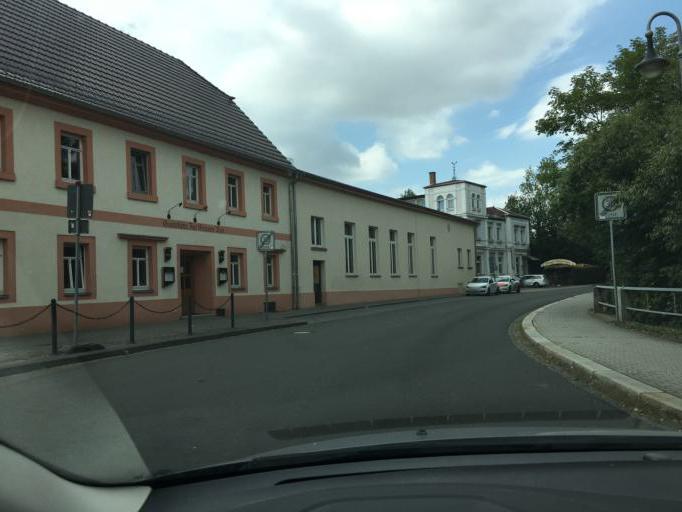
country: DE
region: Saxony
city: Frohburg
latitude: 51.0583
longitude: 12.5581
